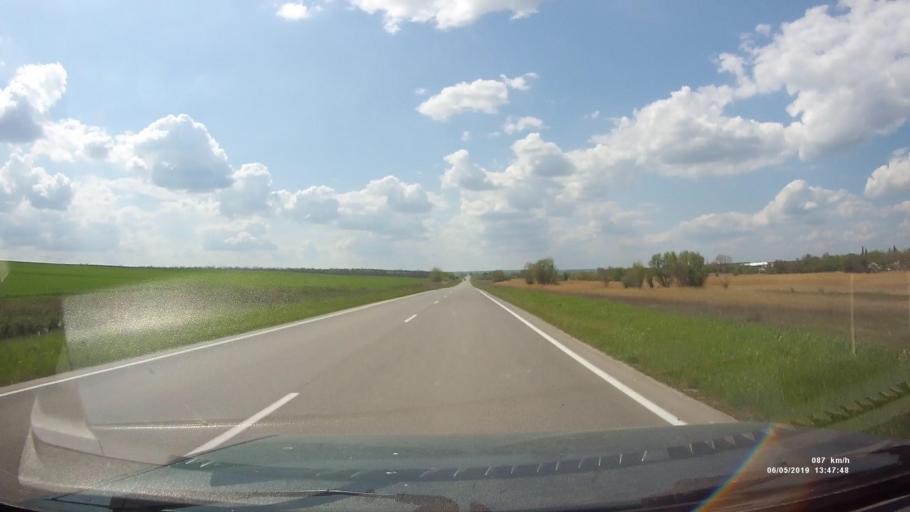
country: RU
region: Rostov
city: Melikhovskaya
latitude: 47.6575
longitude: 40.5565
